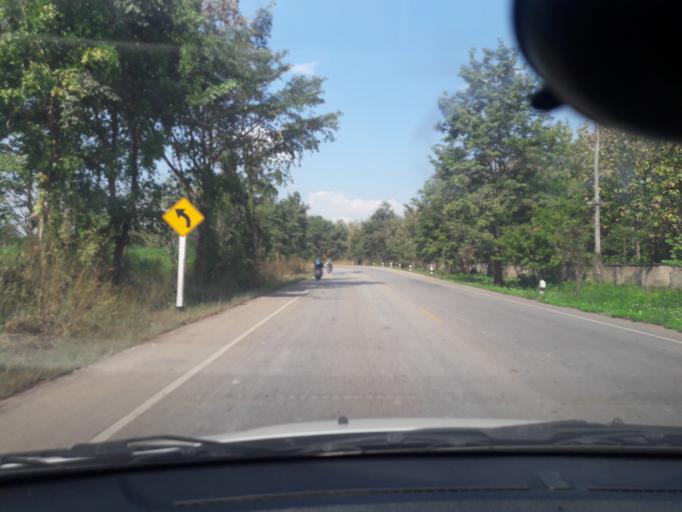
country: TH
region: Lampang
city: Mae Tha
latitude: 18.1967
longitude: 99.5140
